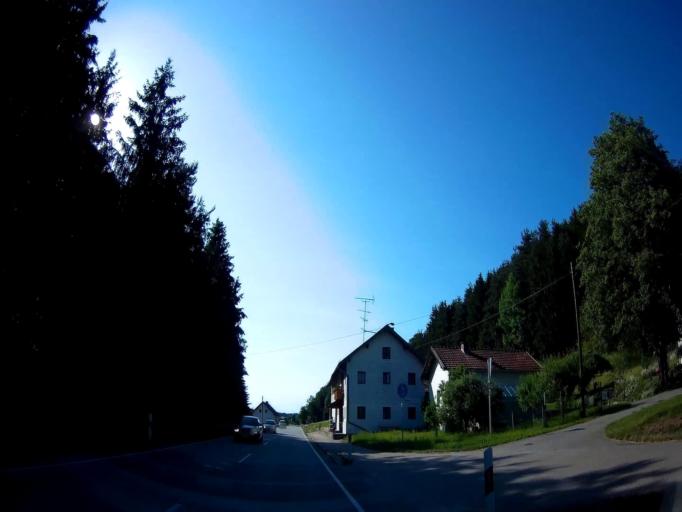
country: DE
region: Bavaria
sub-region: Upper Bavaria
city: Stammham
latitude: 48.2719
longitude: 12.8813
